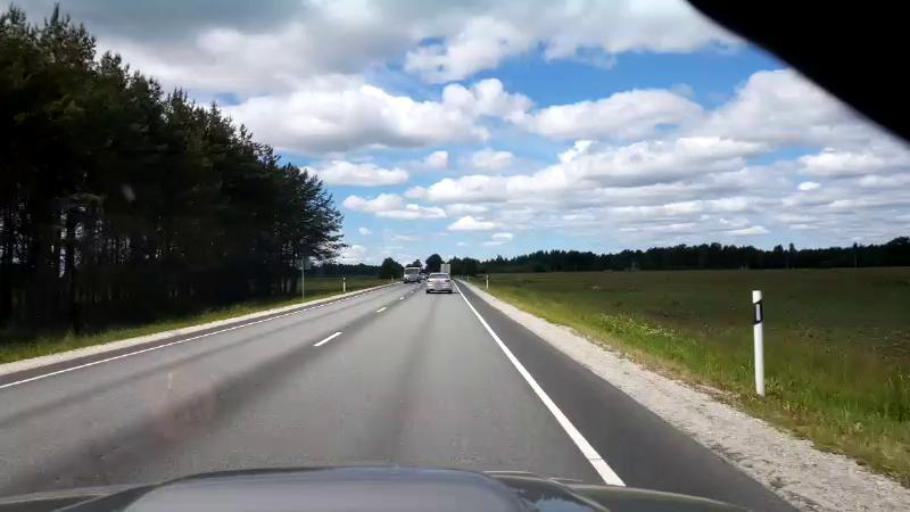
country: EE
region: Paernumaa
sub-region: Halinga vald
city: Parnu-Jaagupi
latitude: 58.6666
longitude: 24.4577
